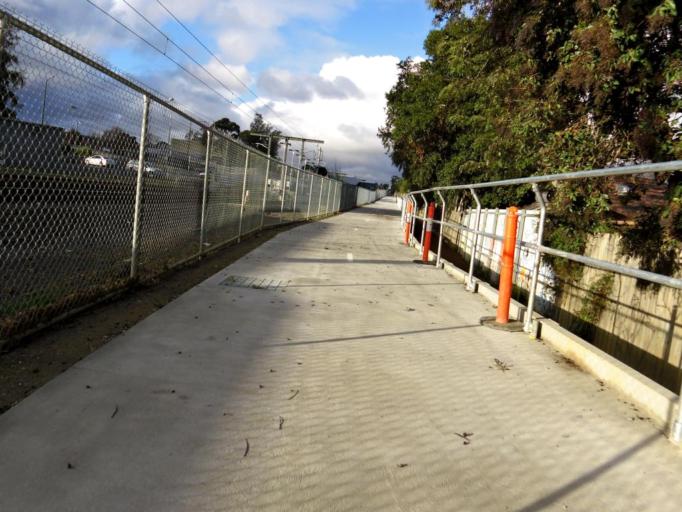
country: AU
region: Victoria
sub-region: Whitehorse
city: Nunawading
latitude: -37.8210
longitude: 145.1724
